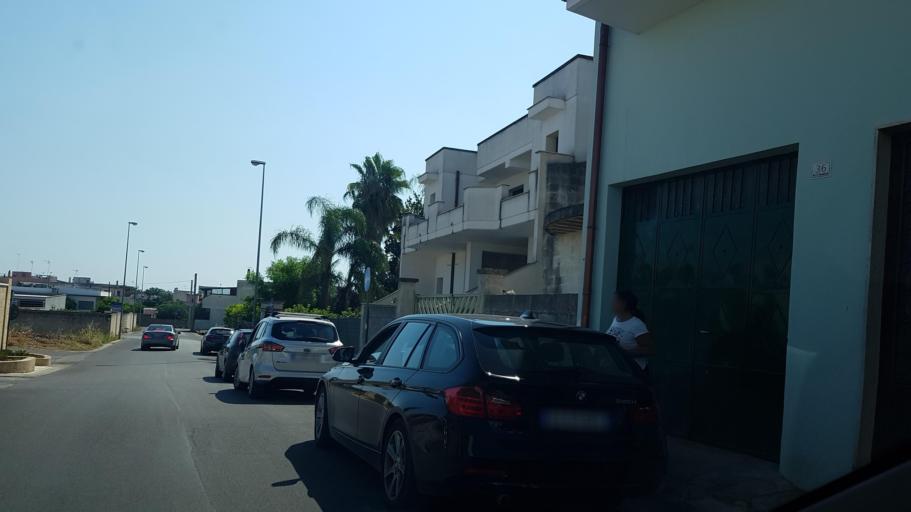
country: IT
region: Apulia
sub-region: Provincia di Lecce
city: Ruffano
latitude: 39.9816
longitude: 18.2509
